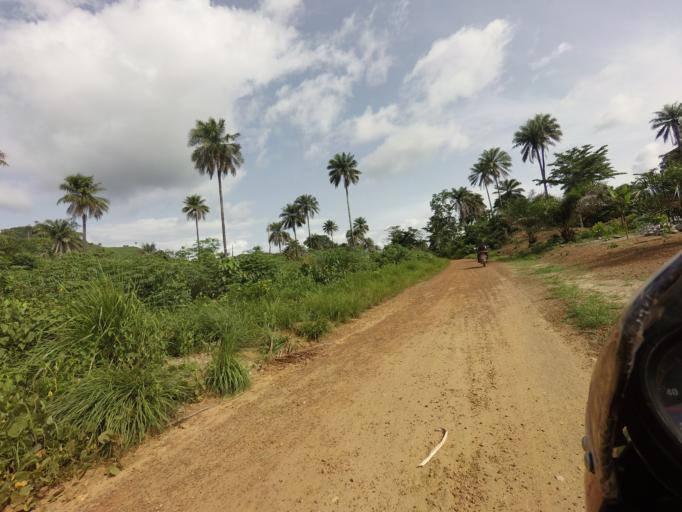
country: SL
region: Eastern Province
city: Jojoima
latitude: 7.8659
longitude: -10.7995
